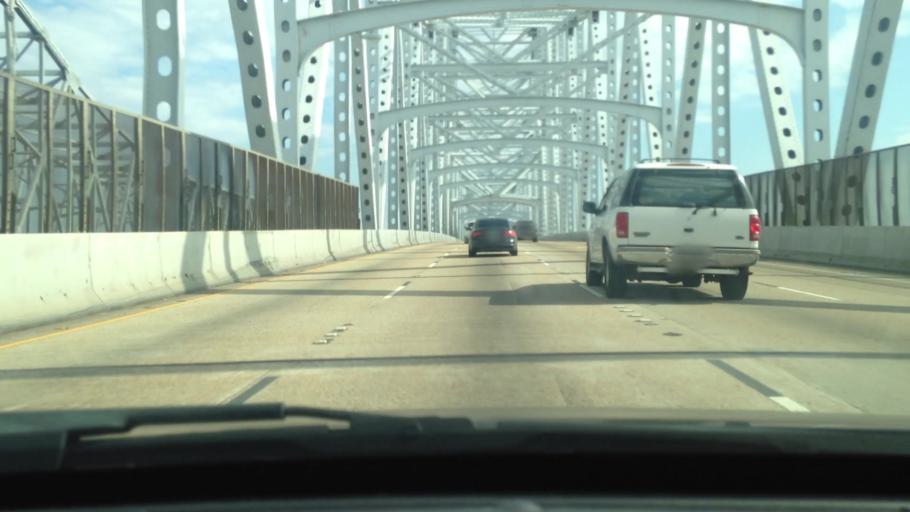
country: US
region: Louisiana
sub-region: Orleans Parish
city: New Orleans
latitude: 29.9377
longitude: -90.0613
